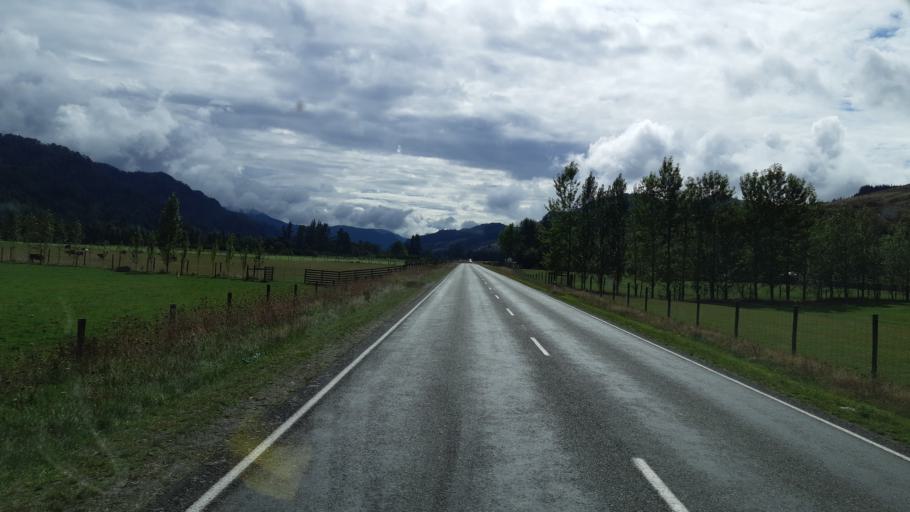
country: NZ
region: West Coast
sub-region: Buller District
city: Westport
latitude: -41.7813
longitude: 172.3735
